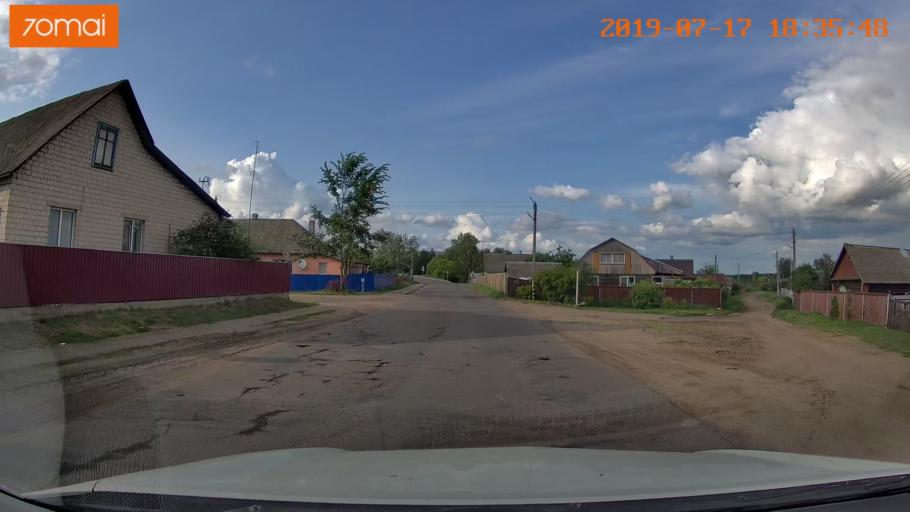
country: BY
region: Mogilev
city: Asipovichy
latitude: 53.2952
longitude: 28.6597
